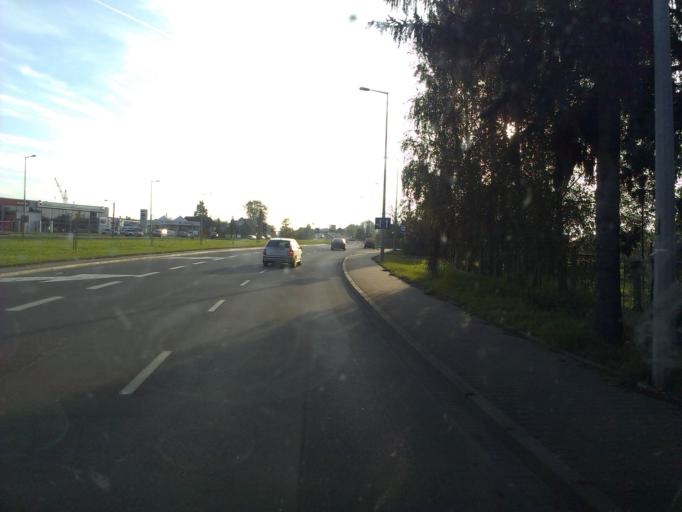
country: PL
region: Lubusz
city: Gorzow Wielkopolski
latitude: 52.7182
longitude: 15.2494
